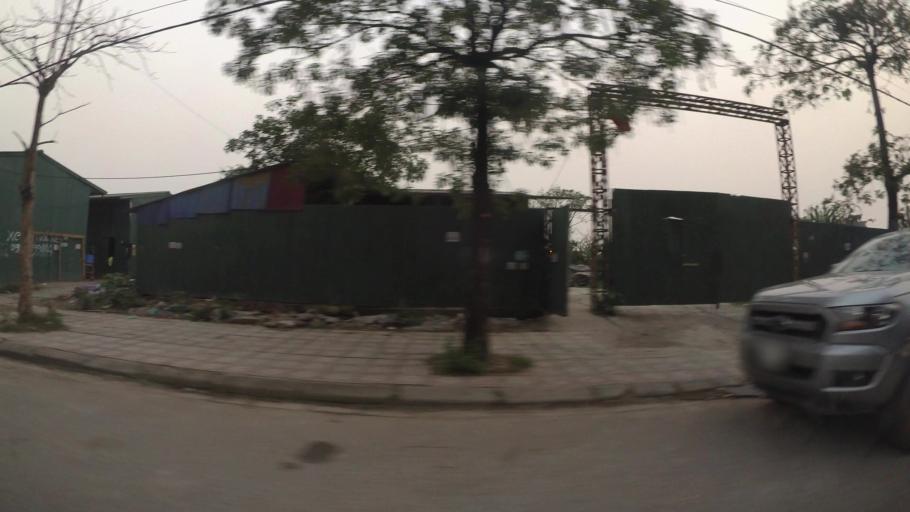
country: VN
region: Ha Noi
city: Tay Ho
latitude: 21.0639
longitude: 105.7904
